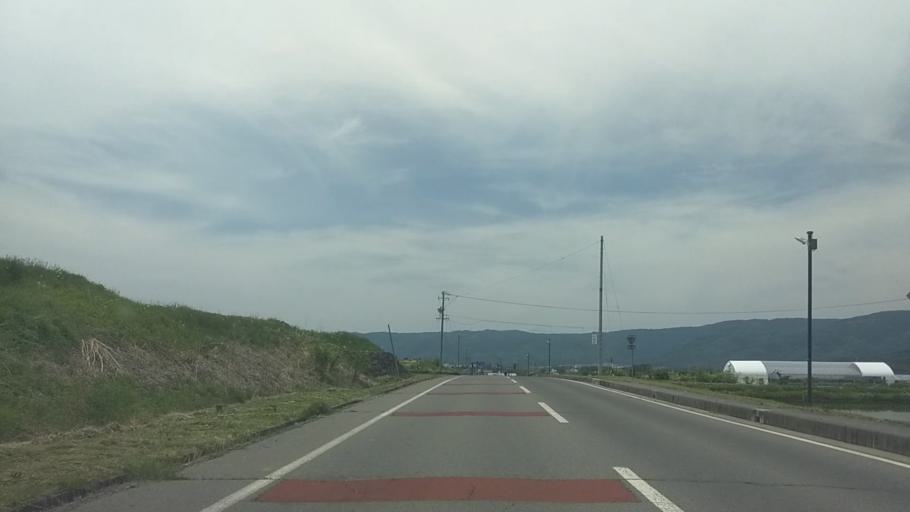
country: JP
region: Nagano
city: Chino
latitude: 36.0249
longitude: 138.2293
